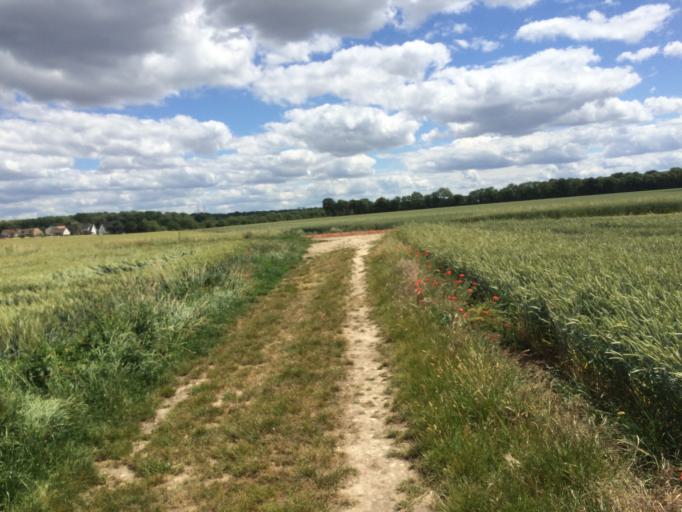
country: FR
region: Ile-de-France
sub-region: Departement de l'Essonne
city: Les Ulis
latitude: 48.6714
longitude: 2.1766
